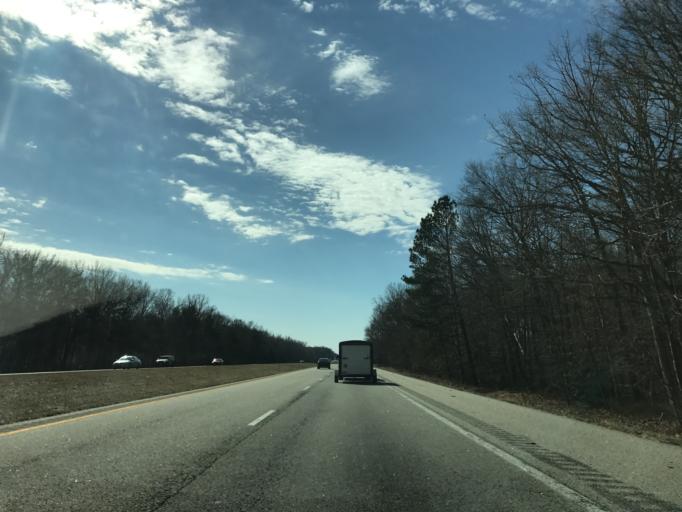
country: US
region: Maryland
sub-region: Queen Anne's County
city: Kingstown
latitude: 39.2231
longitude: -75.8777
